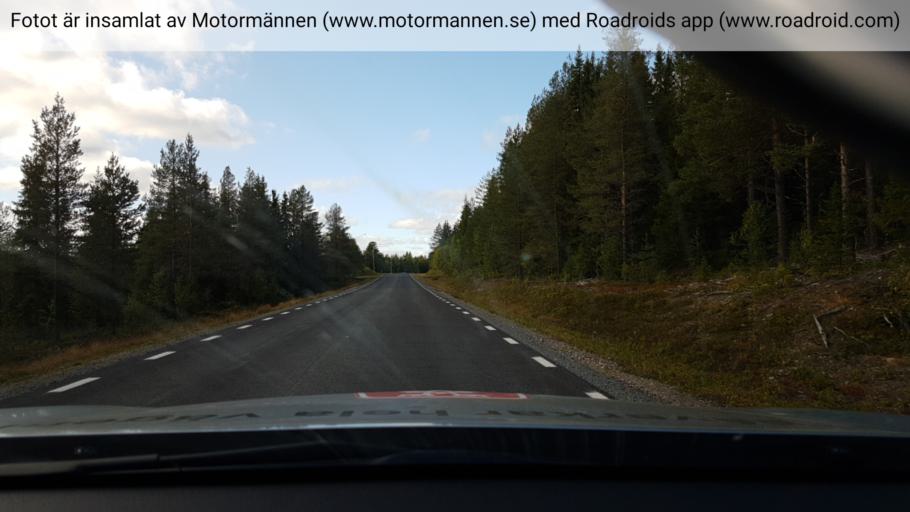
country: SE
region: Vaesterbotten
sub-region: Mala Kommun
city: Mala
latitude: 65.4338
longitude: 18.4754
